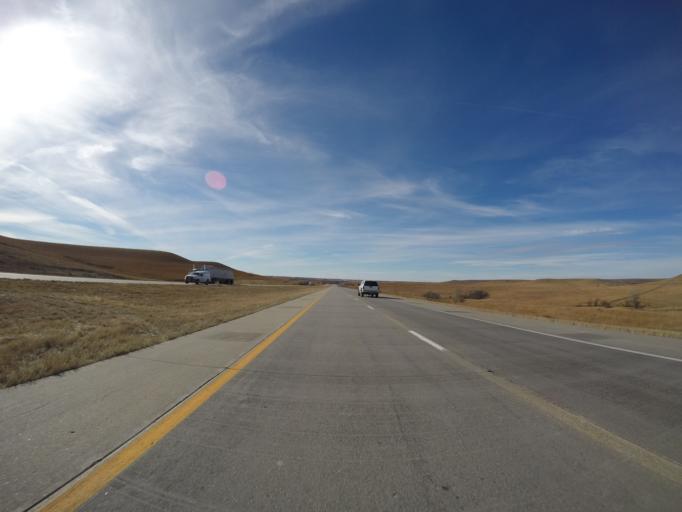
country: US
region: Kansas
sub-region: Riley County
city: Manhattan
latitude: 39.0662
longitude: -96.5928
